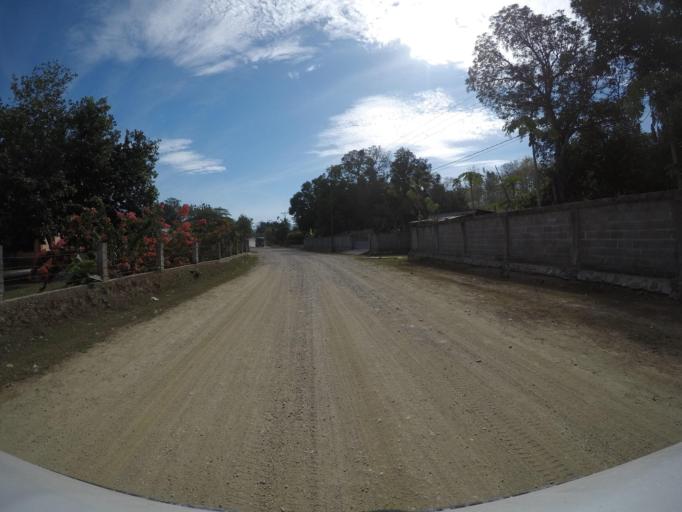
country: TL
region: Bobonaro
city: Maliana
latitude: -8.8830
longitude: 125.2092
